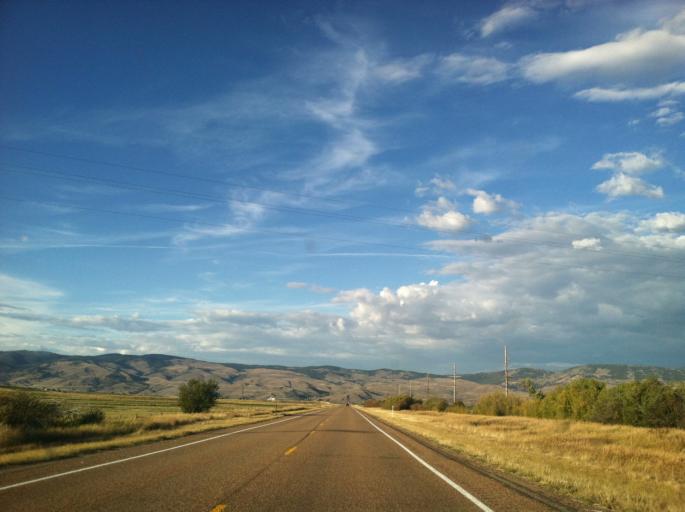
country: US
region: Montana
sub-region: Granite County
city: Philipsburg
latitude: 46.6152
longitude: -113.1766
